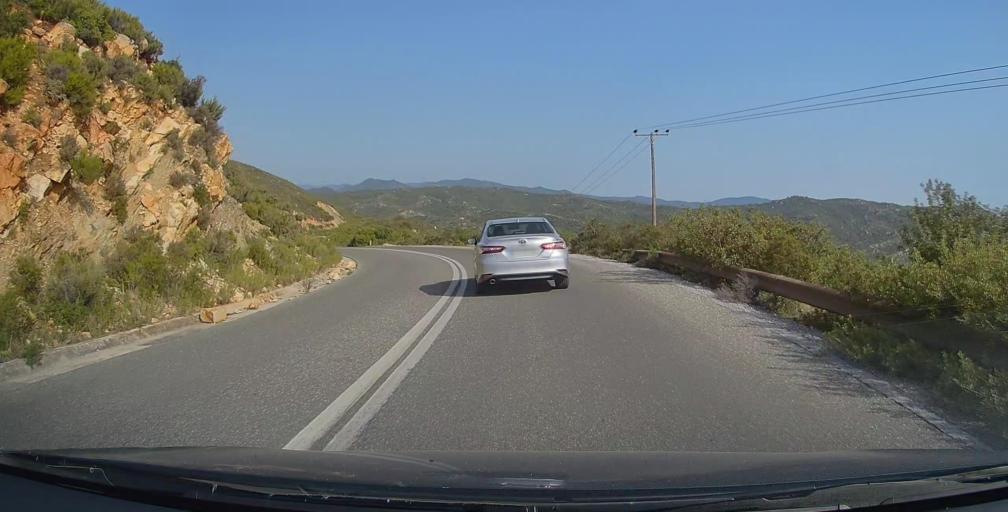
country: GR
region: Central Macedonia
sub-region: Nomos Chalkidikis
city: Sykia
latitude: 39.9858
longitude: 23.9601
